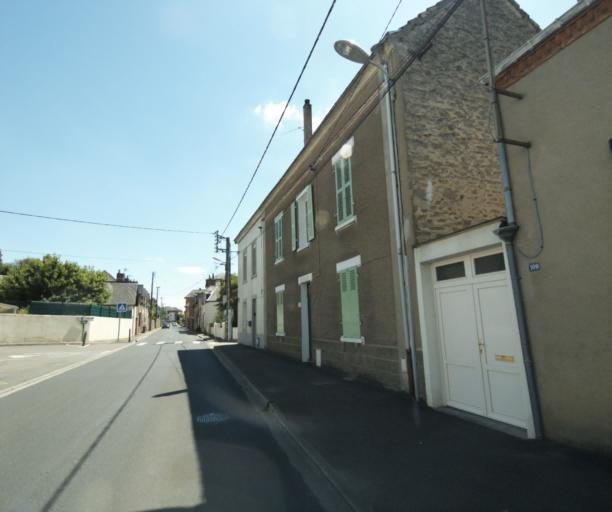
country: FR
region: Pays de la Loire
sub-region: Departement de la Mayenne
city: Laval
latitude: 48.0835
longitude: -0.7706
